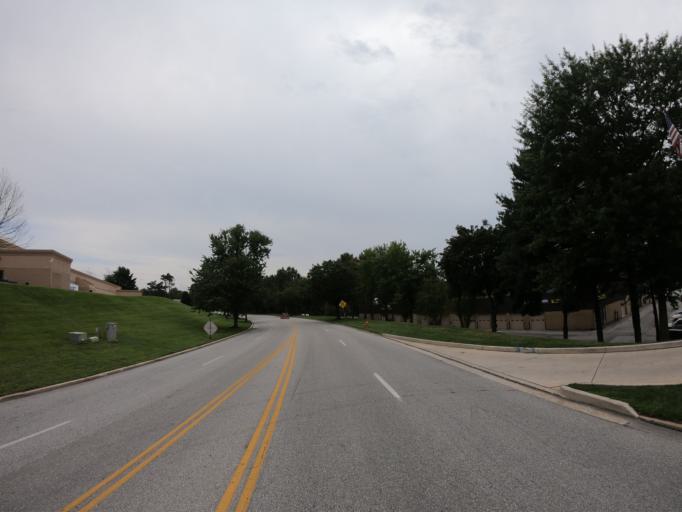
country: US
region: Maryland
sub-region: Howard County
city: Columbia
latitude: 39.1965
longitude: -76.8209
